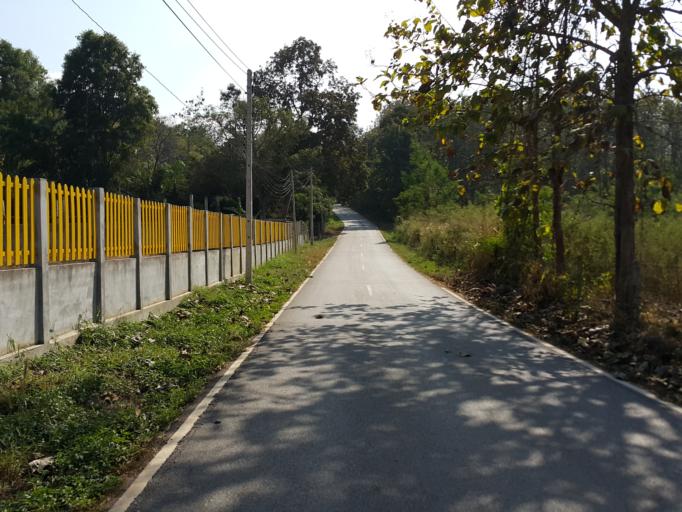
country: TH
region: Chiang Mai
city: Mae On
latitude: 18.8146
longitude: 99.2382
